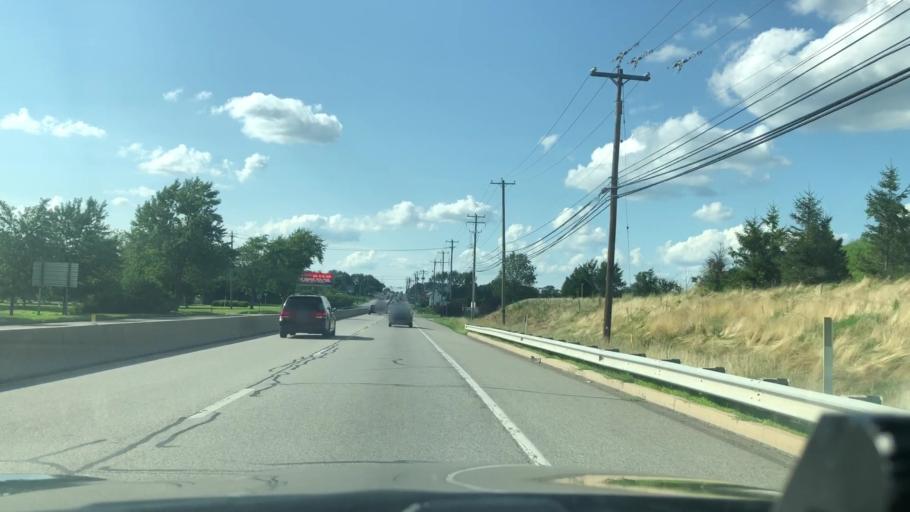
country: US
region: Pennsylvania
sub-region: Montgomery County
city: Spring House
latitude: 40.2118
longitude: -75.2254
